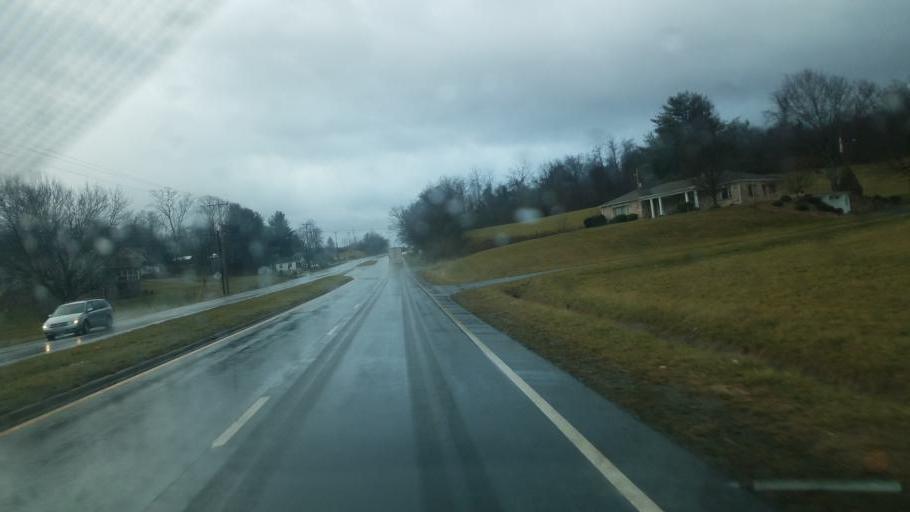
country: US
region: Virginia
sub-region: Giles County
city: Pearisburg
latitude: 37.3157
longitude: -80.7323
